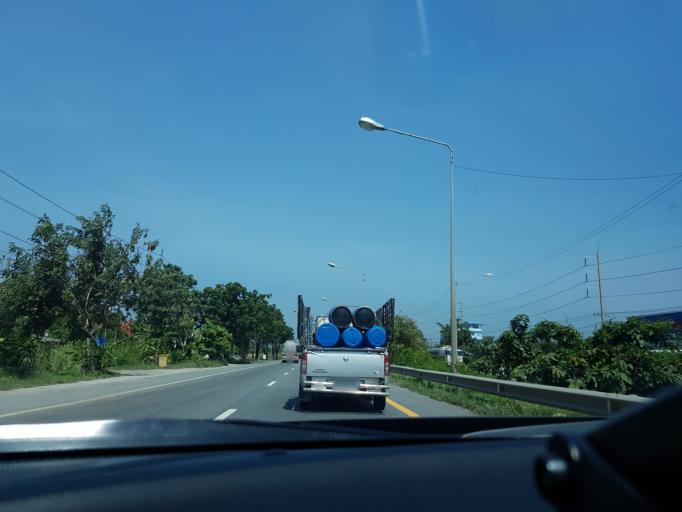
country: TH
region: Sara Buri
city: Saraburi
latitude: 14.5284
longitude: 100.8871
